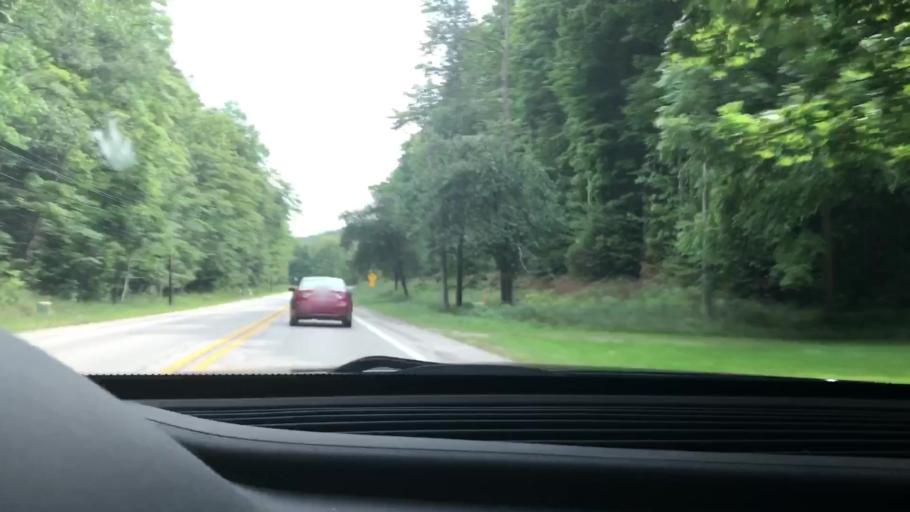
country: US
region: Michigan
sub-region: Antrim County
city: Bellaire
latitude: 45.0815
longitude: -85.2846
